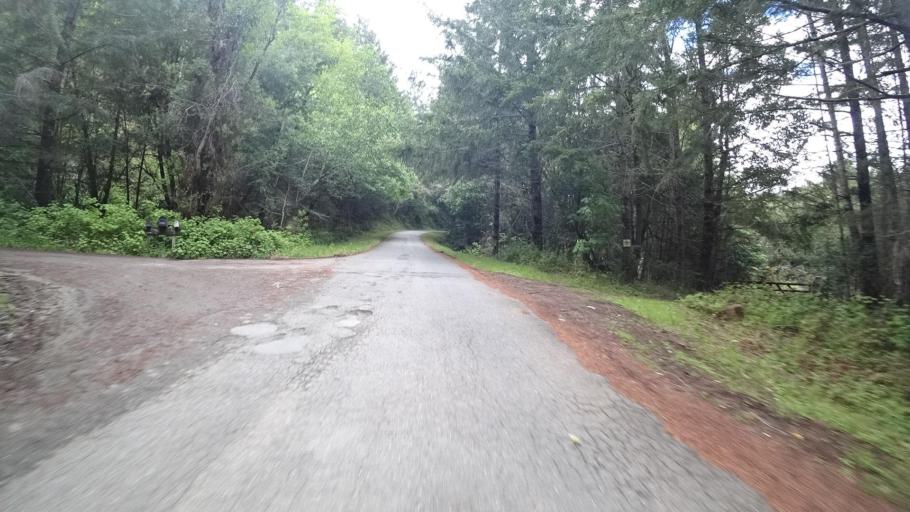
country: US
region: California
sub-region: Humboldt County
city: Blue Lake
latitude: 40.7658
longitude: -123.8902
